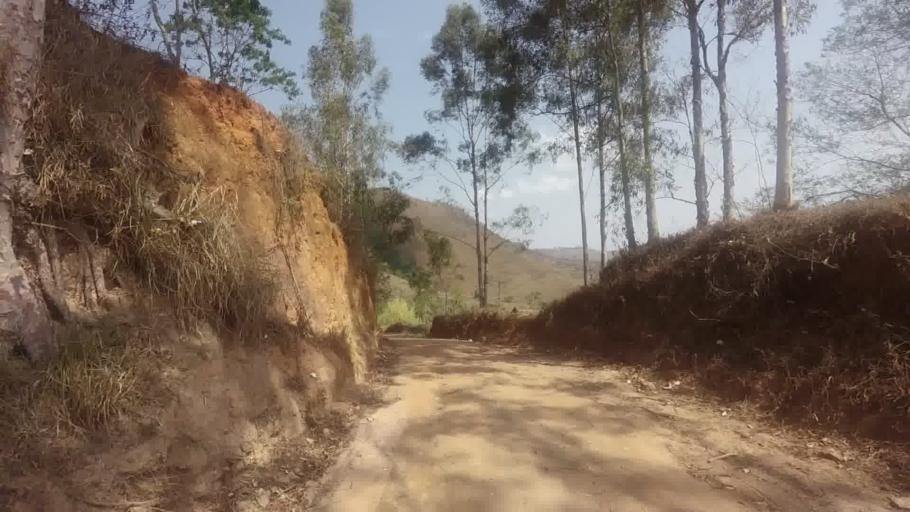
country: BR
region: Espirito Santo
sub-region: Sao Jose Do Calcado
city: Sao Jose do Calcado
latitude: -21.0059
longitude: -41.5088
